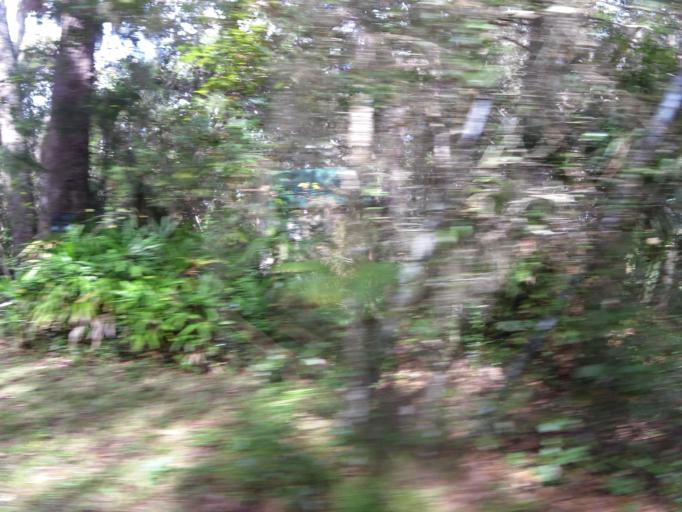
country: US
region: Florida
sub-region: Saint Johns County
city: Villano Beach
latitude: 29.9811
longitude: -81.3965
